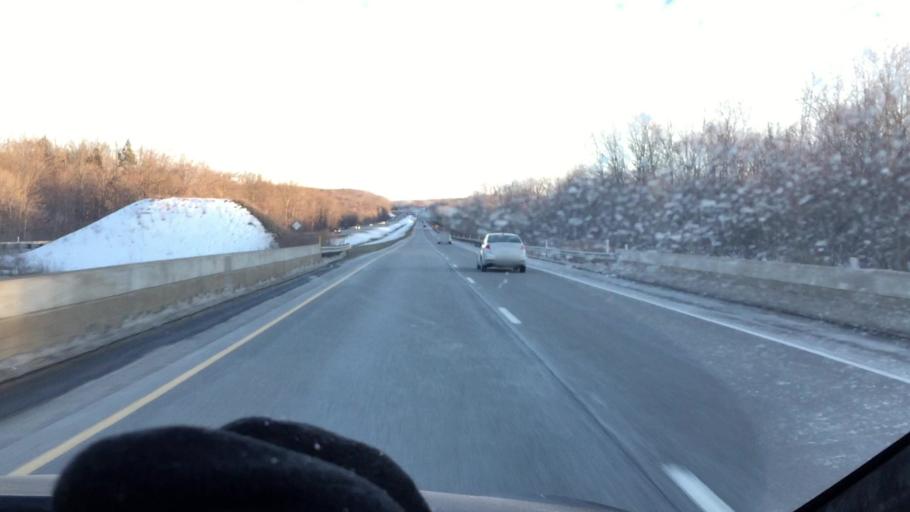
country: US
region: Pennsylvania
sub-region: Crawford County
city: Meadville
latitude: 41.6624
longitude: -80.2073
